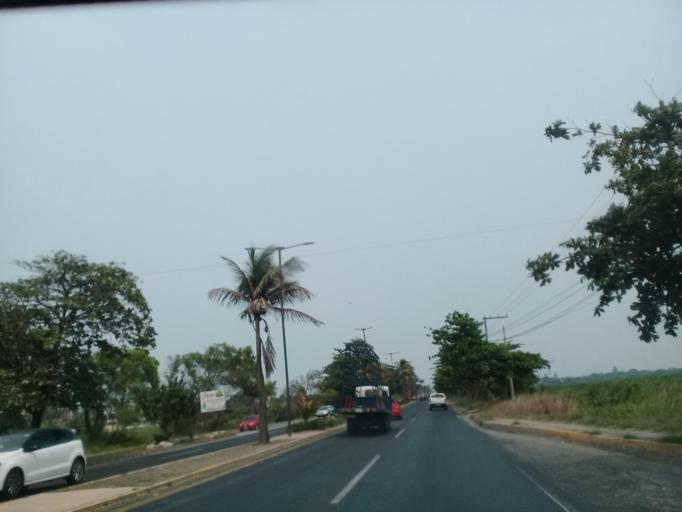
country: MX
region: Veracruz
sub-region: Veracruz
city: Hacienda Sotavento
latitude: 19.1470
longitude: -96.1671
